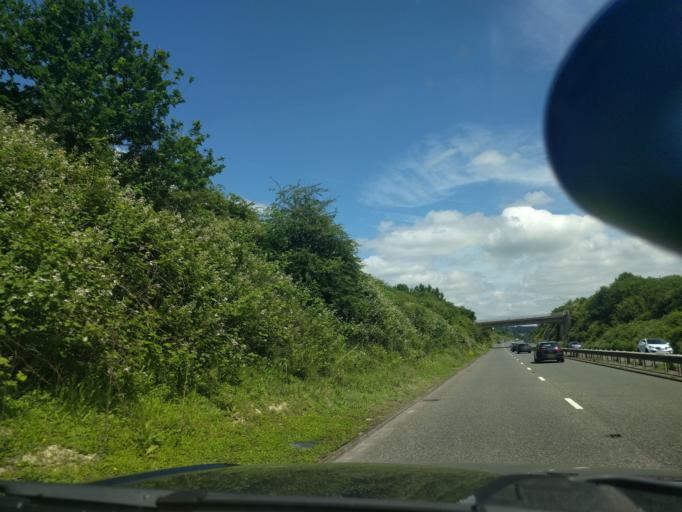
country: GB
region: England
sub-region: Bath and North East Somerset
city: Bath
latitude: 51.3974
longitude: -2.3251
